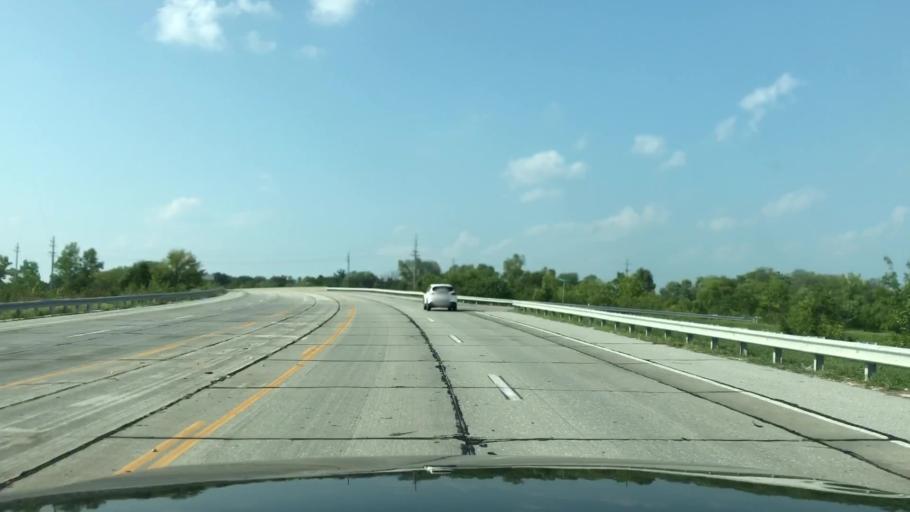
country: US
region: Missouri
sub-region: Saint Charles County
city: Lake Saint Louis
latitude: 38.8071
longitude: -90.8074
